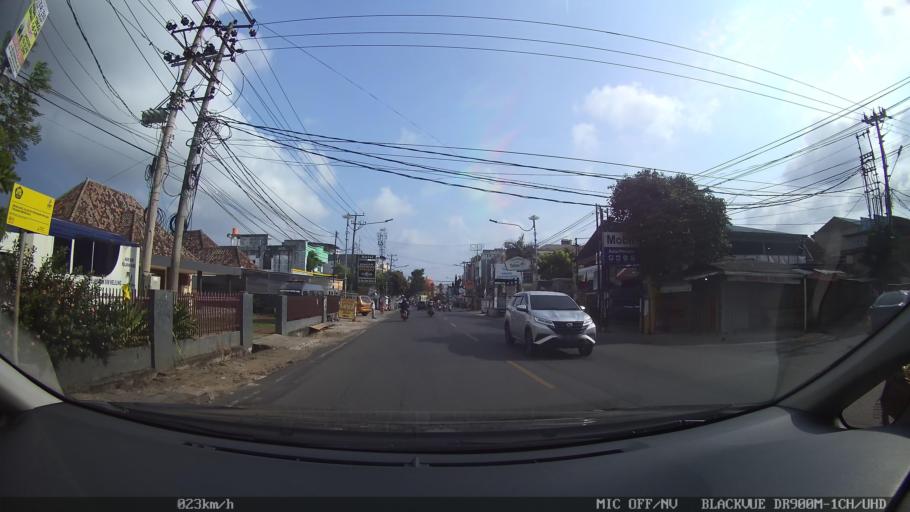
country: ID
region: Lampung
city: Bandarlampung
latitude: -5.4245
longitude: 105.2515
